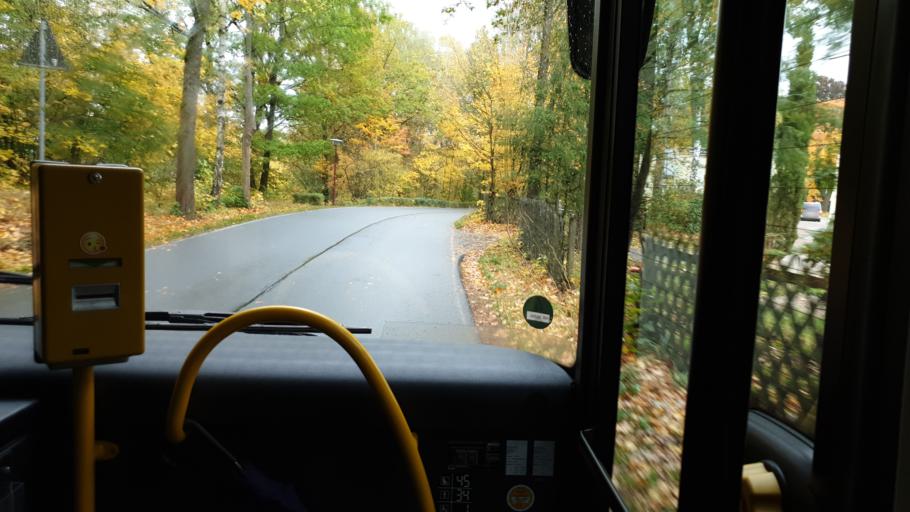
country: DE
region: Saxony
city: Kurort Gohrisch
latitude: 50.9068
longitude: 14.1107
